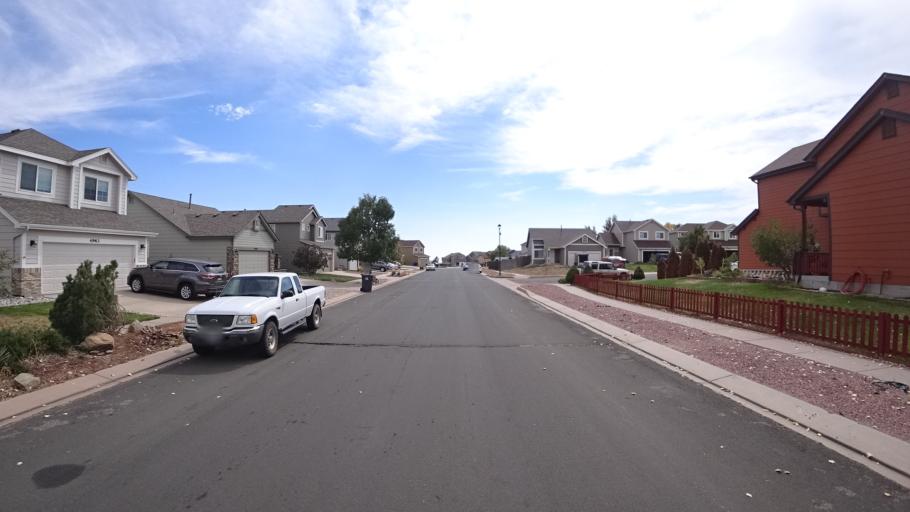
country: US
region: Colorado
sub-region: El Paso County
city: Cimarron Hills
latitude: 38.9028
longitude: -104.7179
